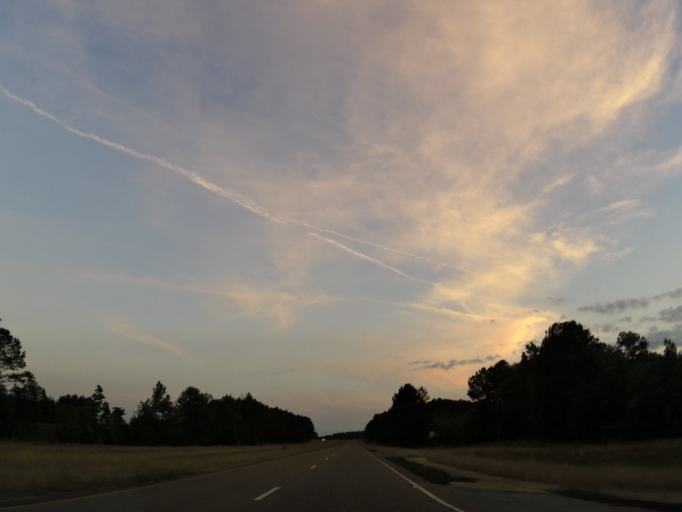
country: US
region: Mississippi
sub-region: Kemper County
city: De Kalb
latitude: 32.6929
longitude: -88.4871
